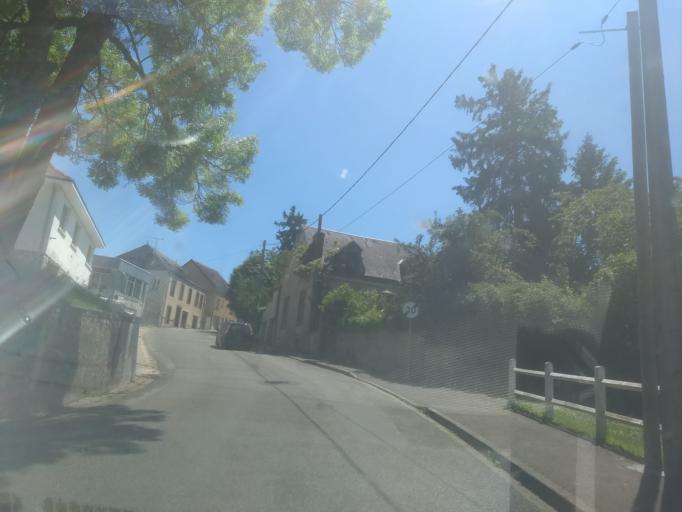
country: FR
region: Centre
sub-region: Departement d'Eure-et-Loir
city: Nogent-le-Rotrou
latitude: 48.3189
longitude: 0.8239
